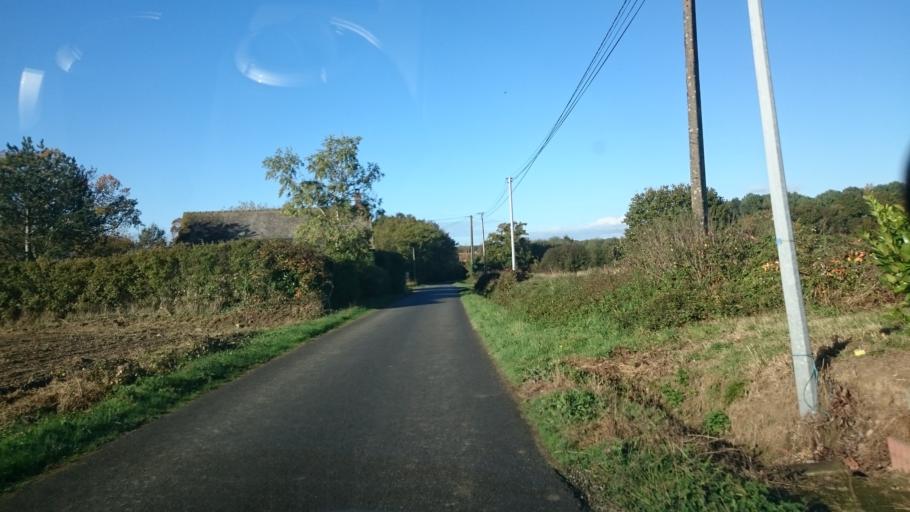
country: FR
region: Brittany
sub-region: Departement d'Ille-et-Vilaine
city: Crevin
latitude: 47.9464
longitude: -1.6909
